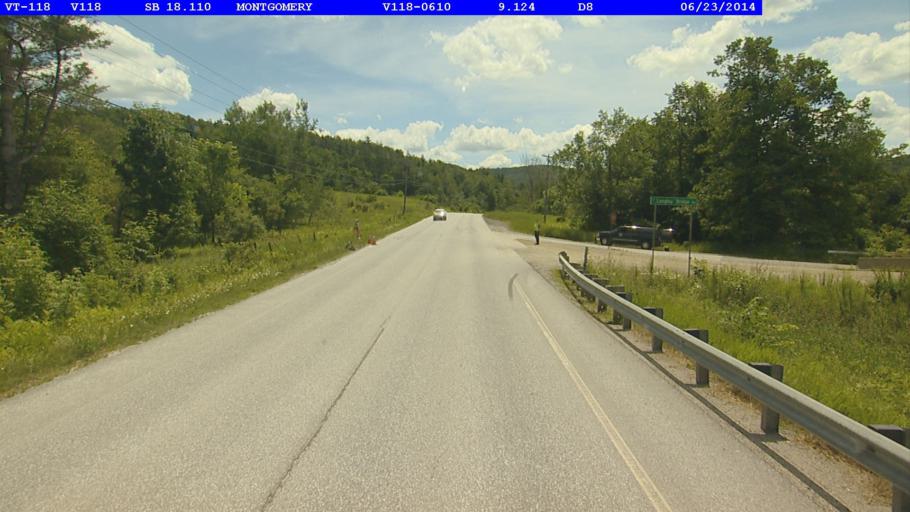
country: US
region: Vermont
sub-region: Franklin County
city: Richford
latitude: 44.9077
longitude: -72.6553
